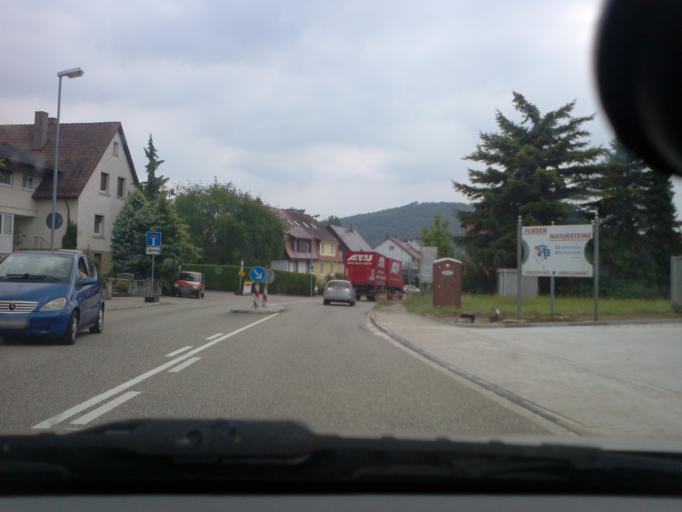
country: DE
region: Baden-Wuerttemberg
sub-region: Karlsruhe Region
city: Weingarten
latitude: 49.0099
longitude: 8.5324
